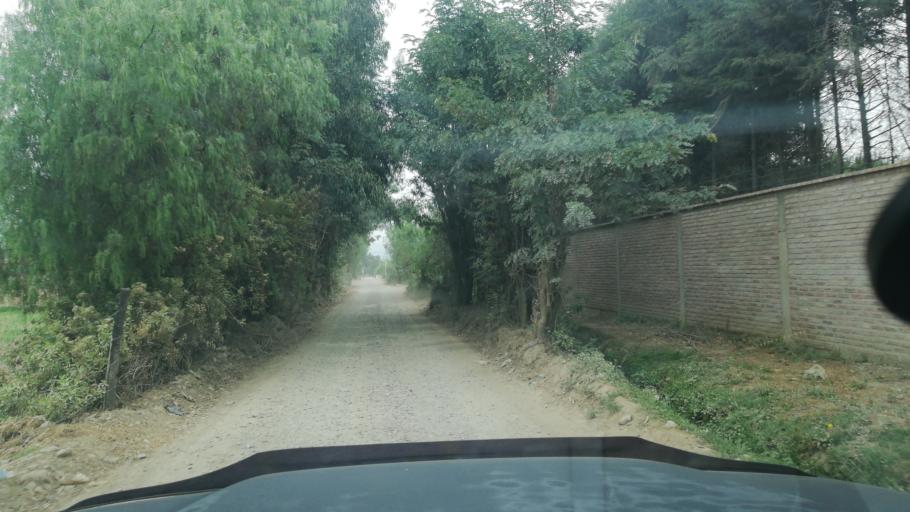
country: BO
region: Cochabamba
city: Cochabamba
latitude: -17.3549
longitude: -66.2203
